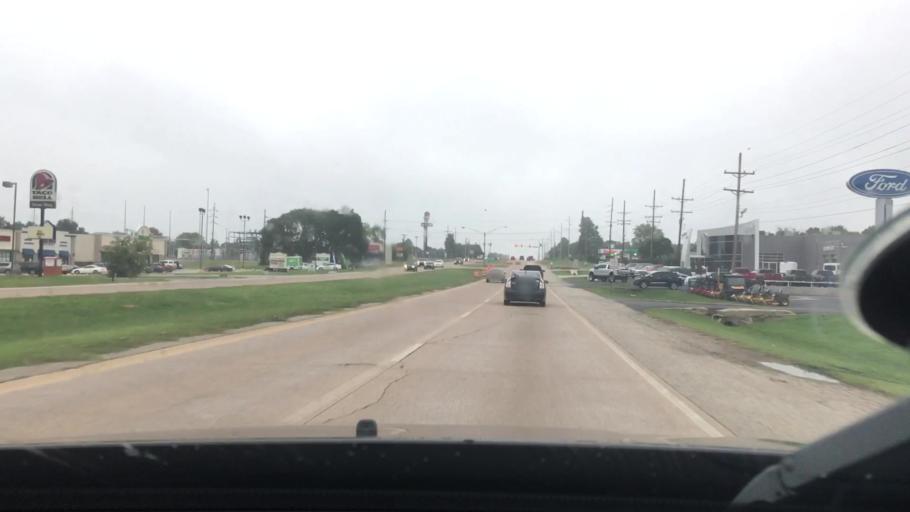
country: US
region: Oklahoma
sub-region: Seminole County
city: Seminole
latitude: 35.2431
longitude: -96.6710
